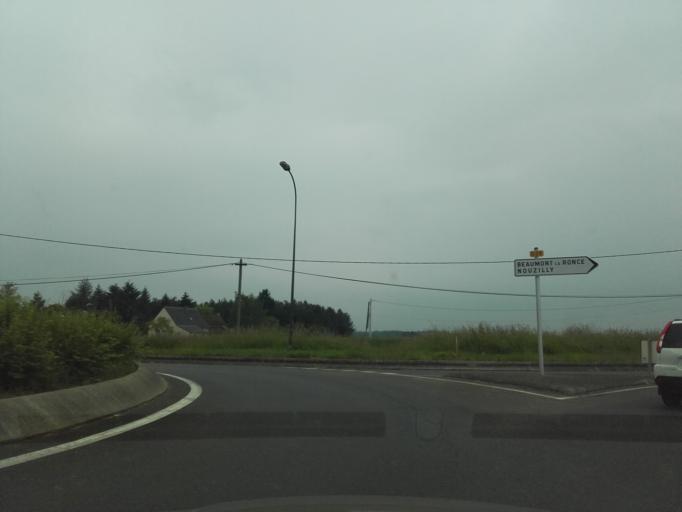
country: FR
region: Centre
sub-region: Departement d'Indre-et-Loire
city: Beaumont-la-Ronce
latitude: 47.5659
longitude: 0.6772
